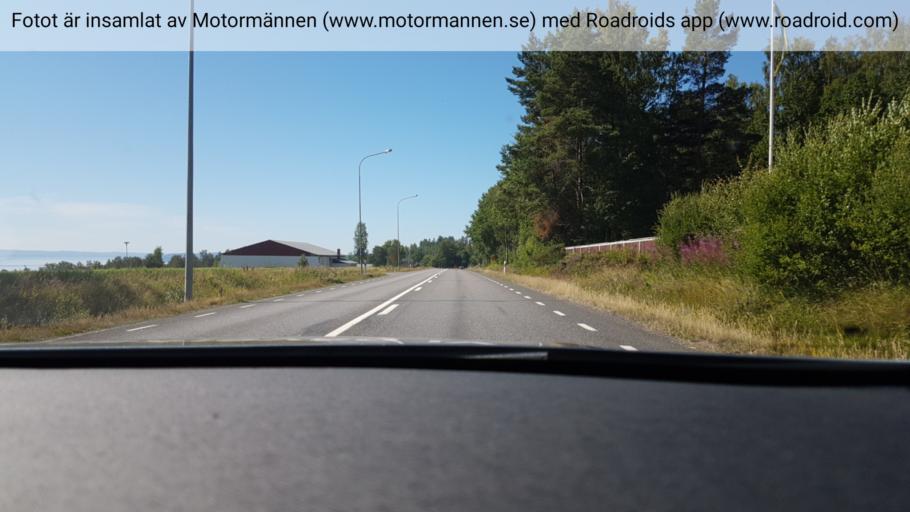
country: SE
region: Joenkoeping
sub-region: Habo Kommun
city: Habo
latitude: 57.9977
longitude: 14.1184
